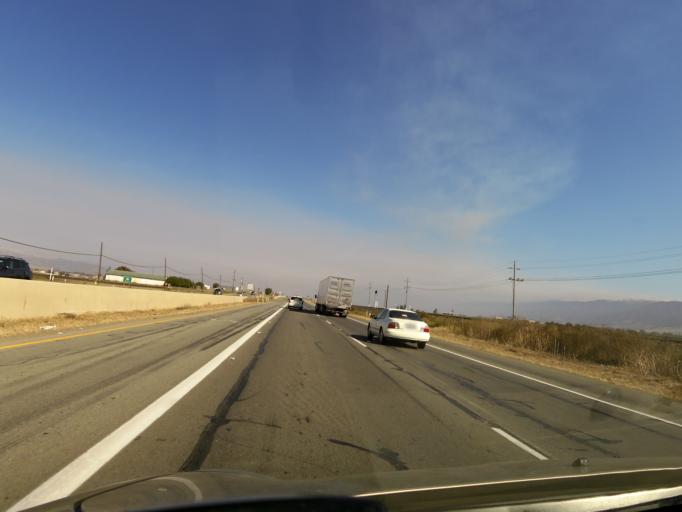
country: US
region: California
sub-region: Monterey County
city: Chualar
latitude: 36.6236
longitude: -121.5821
